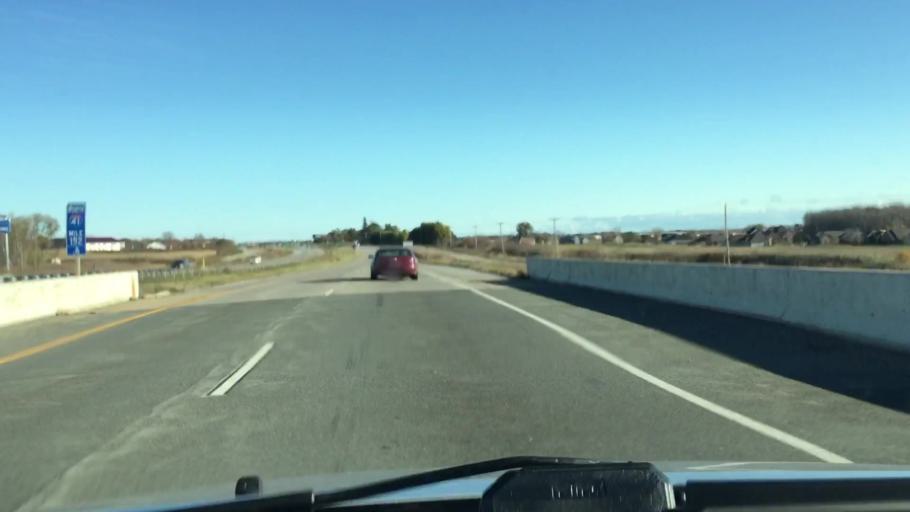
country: US
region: Wisconsin
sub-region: Brown County
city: Wrightstown
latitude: 44.3287
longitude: -88.2103
